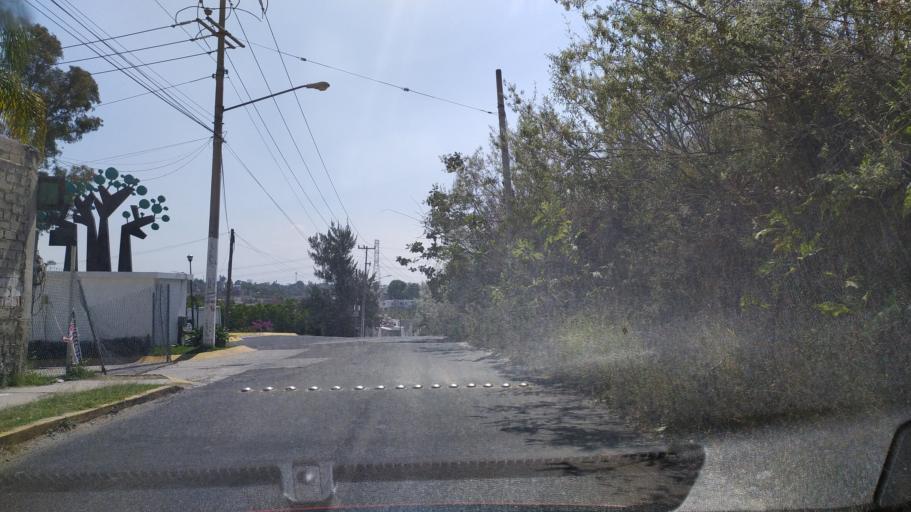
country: MX
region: Jalisco
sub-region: Zapopan
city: Campo Real
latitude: 20.7739
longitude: -103.4342
